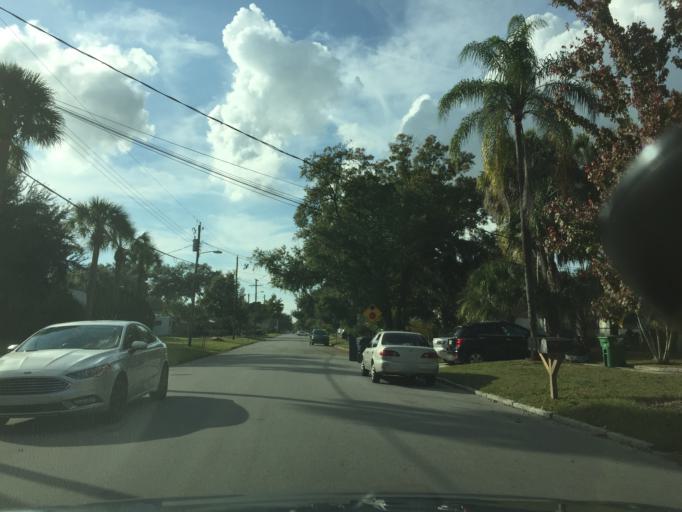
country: US
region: Florida
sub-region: Hillsborough County
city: Tampa
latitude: 27.9459
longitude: -82.4879
